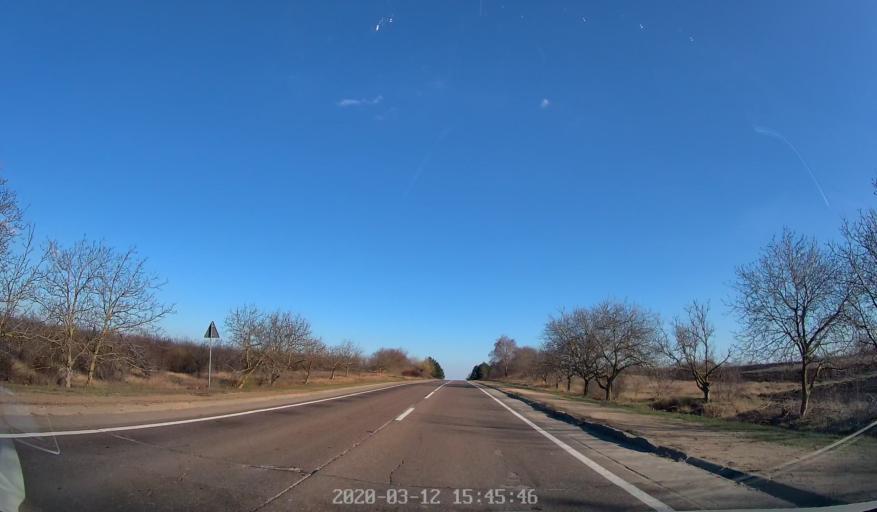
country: MD
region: Chisinau
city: Stauceni
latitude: 47.1038
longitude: 28.8809
